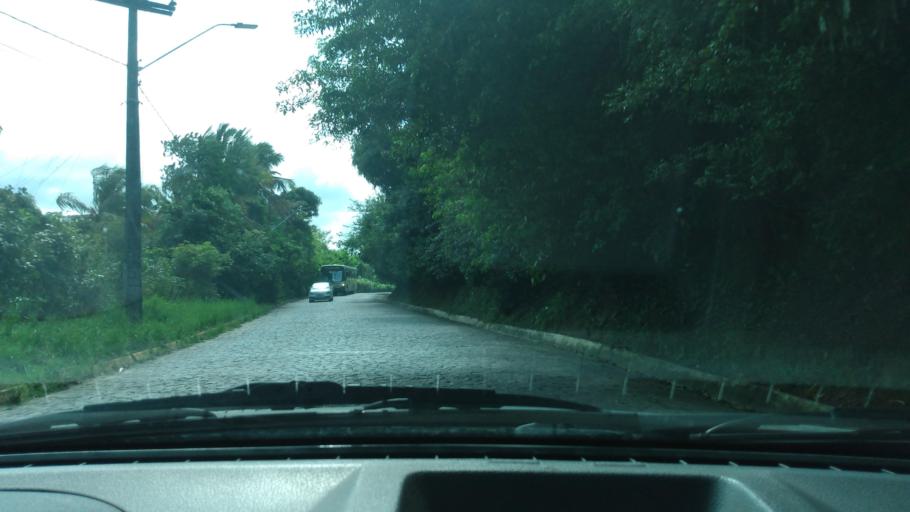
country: BR
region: Pernambuco
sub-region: Cabo De Santo Agostinho
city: Cabo
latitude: -8.3527
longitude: -34.9517
